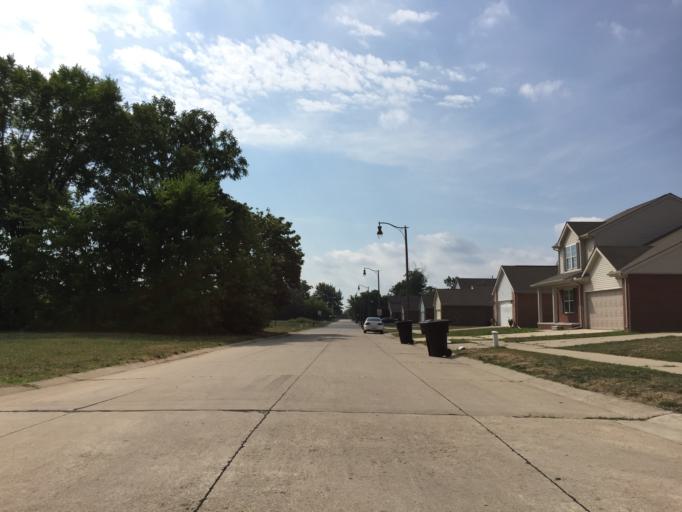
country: US
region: Michigan
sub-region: Wayne County
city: Grosse Pointe Park
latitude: 42.3641
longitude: -82.9717
